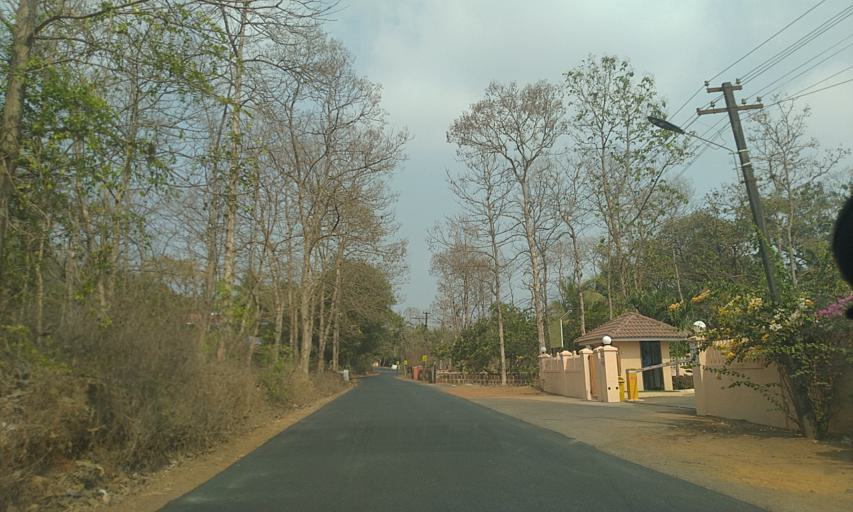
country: IN
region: Goa
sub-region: South Goa
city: Raia
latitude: 15.3078
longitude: 73.9646
